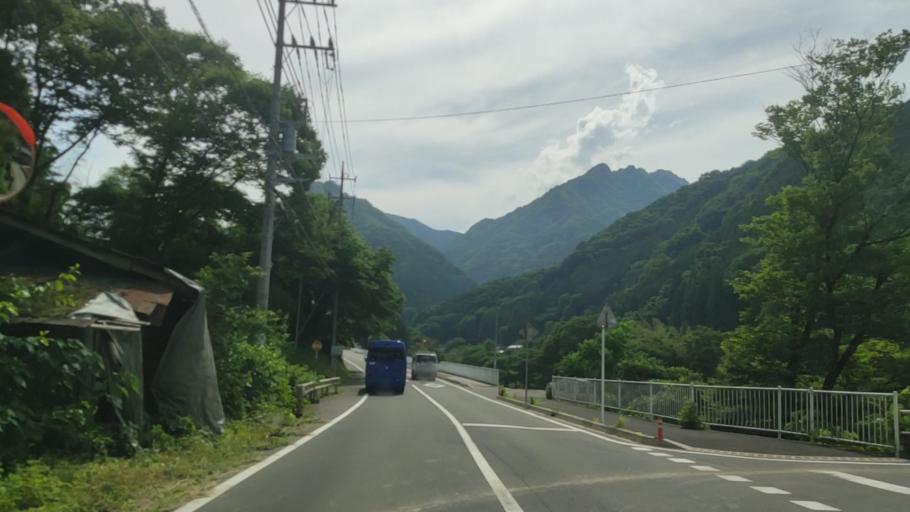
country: JP
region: Gunma
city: Tomioka
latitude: 36.1994
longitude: 138.7618
